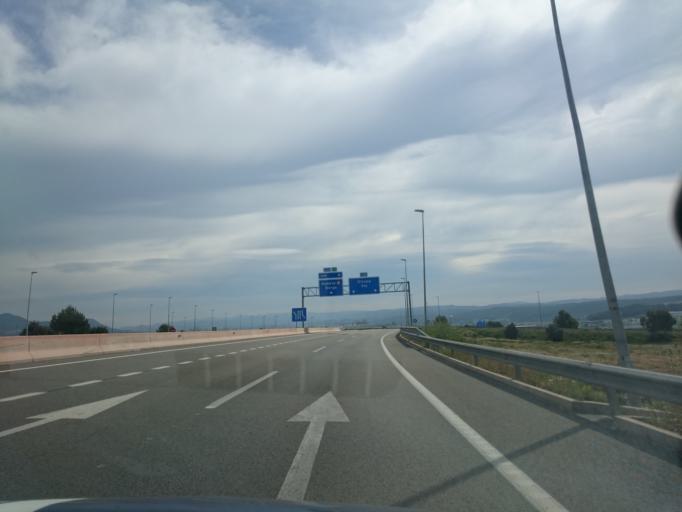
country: ES
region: Catalonia
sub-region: Provincia de Barcelona
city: Sant Fruitos de Bages
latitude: 41.7789
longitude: 1.8827
